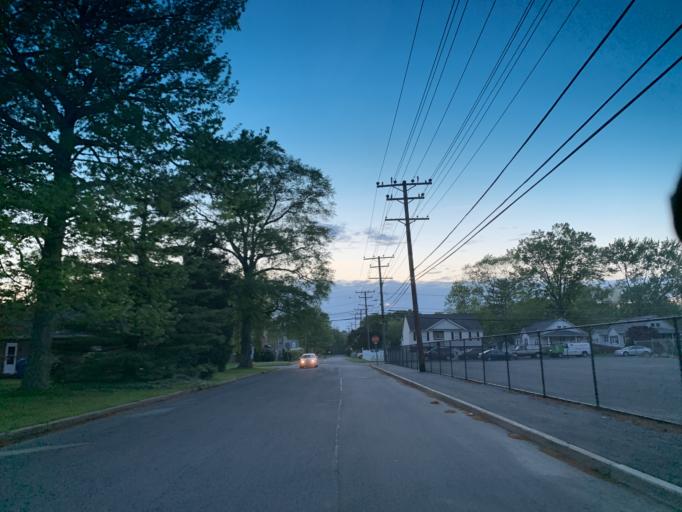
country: US
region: Maryland
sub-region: Harford County
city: Aberdeen
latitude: 39.5072
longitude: -76.1715
